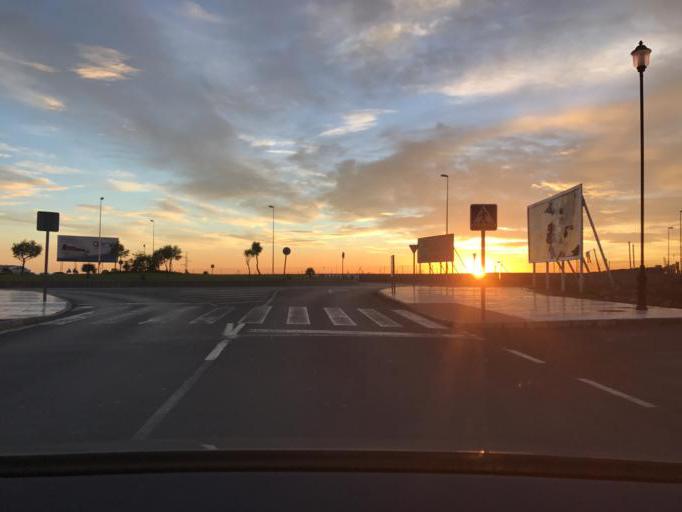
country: ES
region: Andalusia
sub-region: Provincia de Almeria
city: Aguadulce
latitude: 36.8218
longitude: -2.5828
